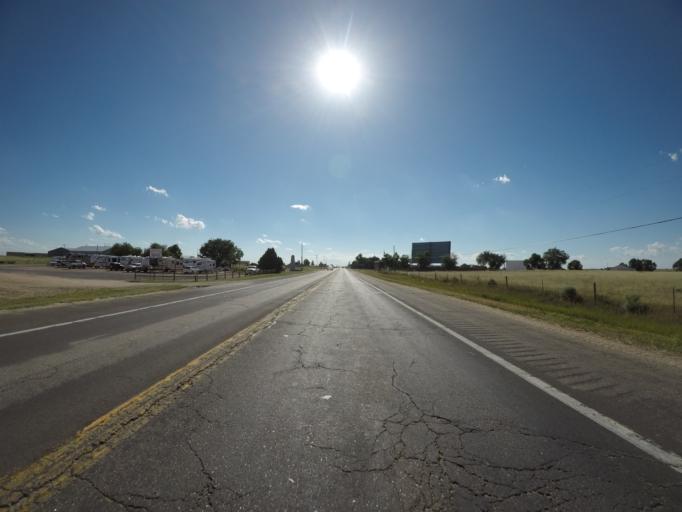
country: US
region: Colorado
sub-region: Logan County
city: Sterling
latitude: 40.6237
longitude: -103.2617
